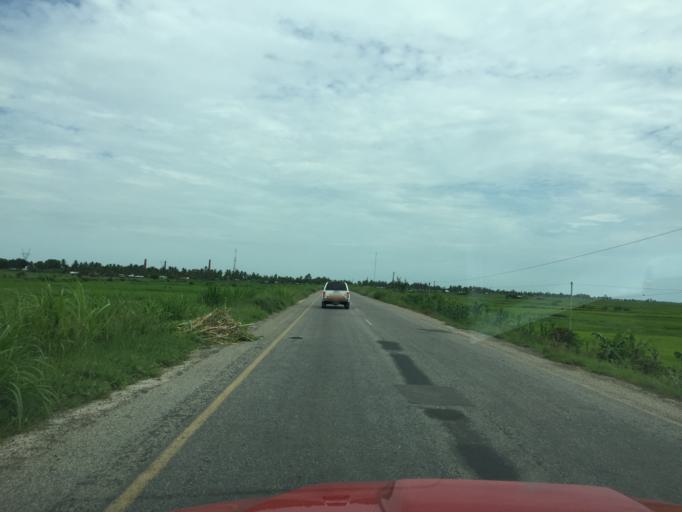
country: MZ
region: Zambezia
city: Quelimane
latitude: -17.7235
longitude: 36.8994
